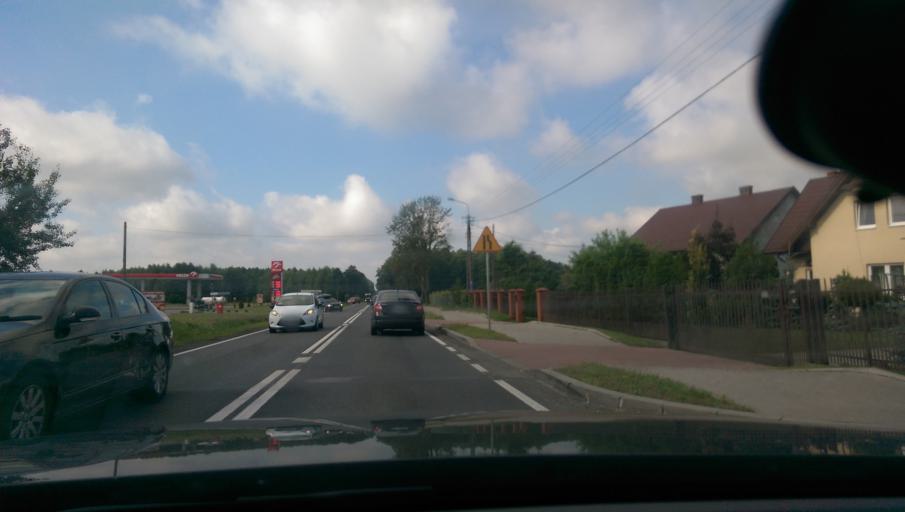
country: PL
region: Masovian Voivodeship
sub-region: Powiat ciechanowski
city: Ojrzen
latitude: 52.7611
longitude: 20.5412
